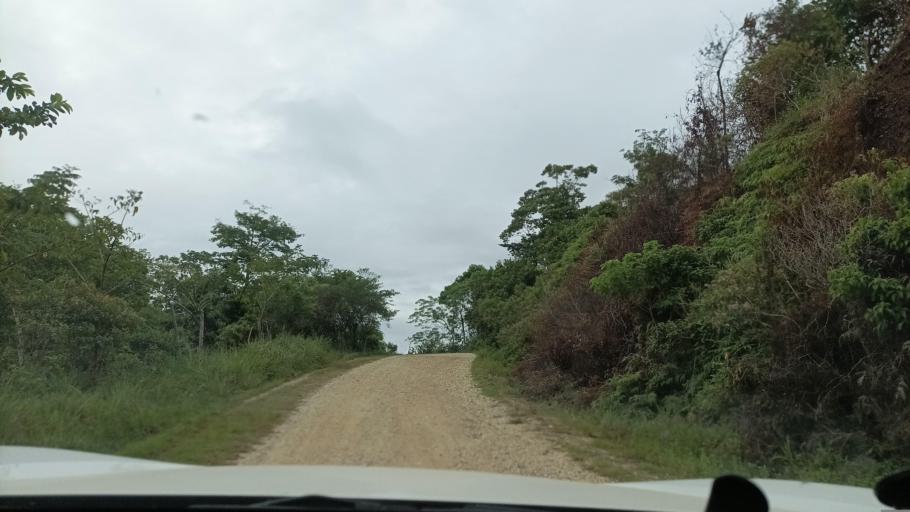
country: MX
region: Veracruz
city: Hidalgotitlan
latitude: 17.5803
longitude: -94.4229
